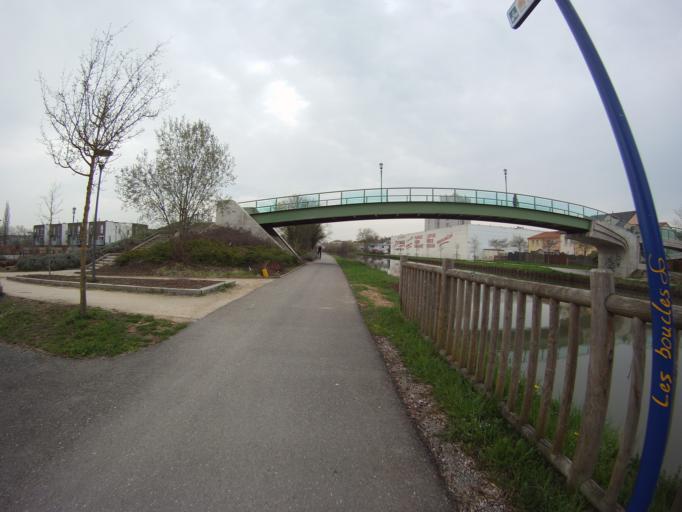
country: FR
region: Lorraine
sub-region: Departement de Meurthe-et-Moselle
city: Jarville-la-Malgrange
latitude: 48.6704
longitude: 6.2090
